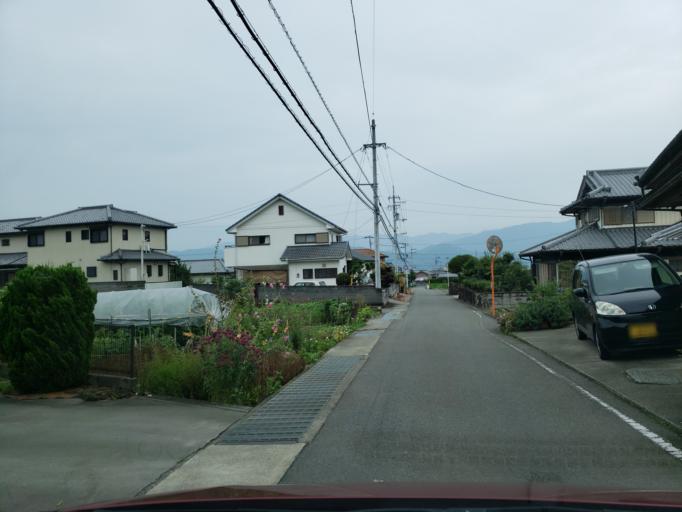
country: JP
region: Tokushima
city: Wakimachi
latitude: 34.0957
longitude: 134.2280
